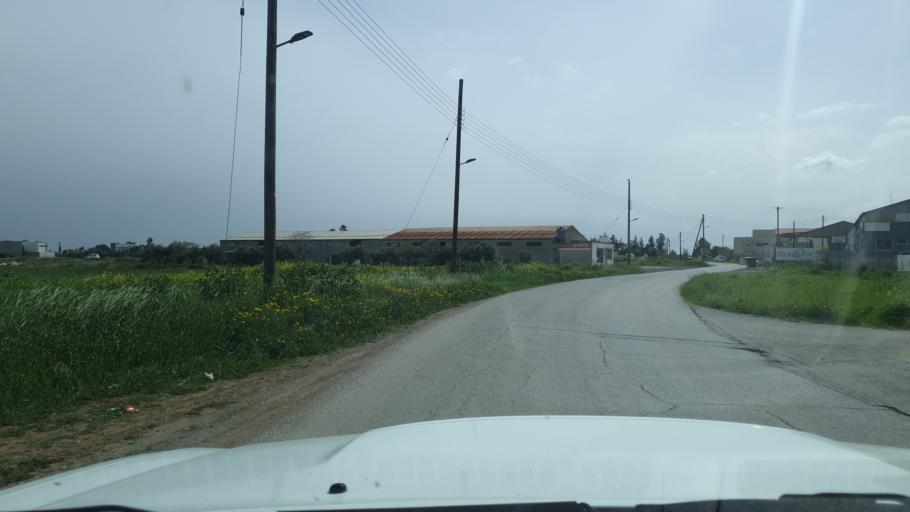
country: CY
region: Lefkosia
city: Geri
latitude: 35.0869
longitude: 33.3872
